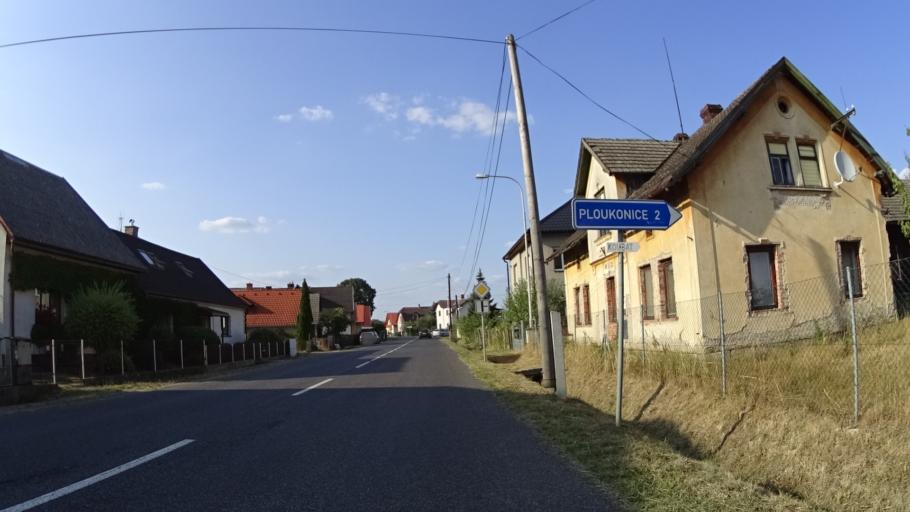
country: CZ
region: Central Bohemia
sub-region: Okres Mlada Boleslav
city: Zd'ar
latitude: 50.5572
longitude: 15.0685
